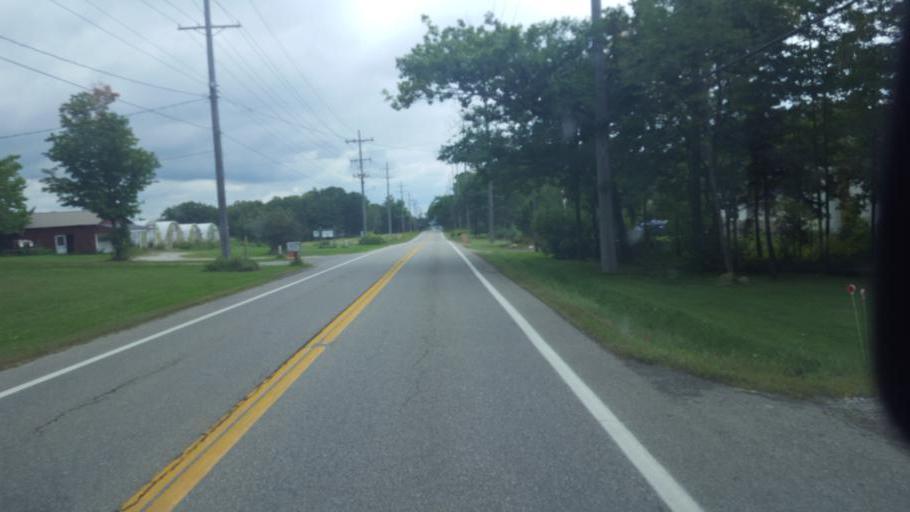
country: US
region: Ohio
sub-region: Geauga County
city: Burton
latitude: 41.5322
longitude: -81.1400
